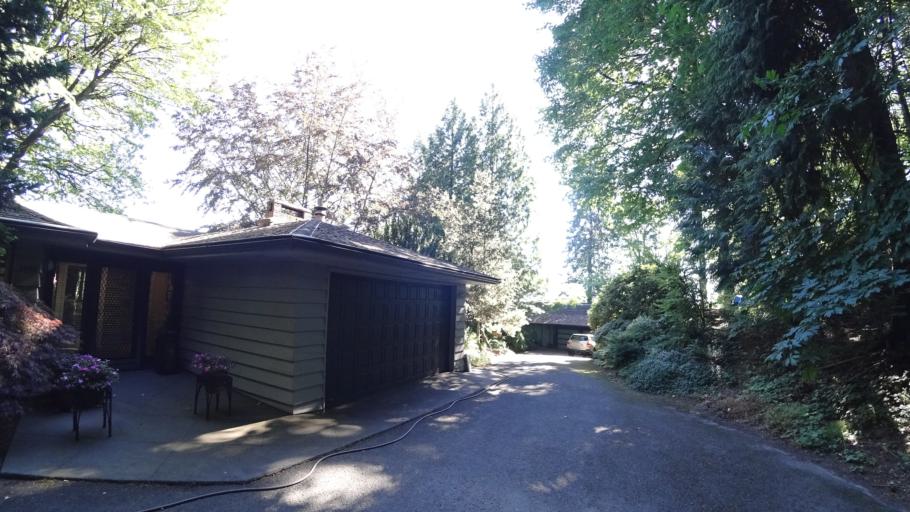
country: US
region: Oregon
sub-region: Multnomah County
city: Portland
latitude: 45.4943
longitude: -122.6807
